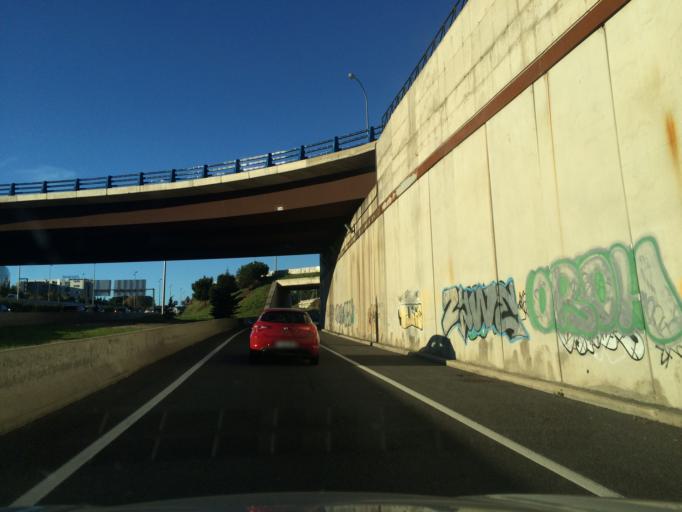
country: ES
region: Madrid
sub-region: Provincia de Madrid
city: Las Tablas
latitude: 40.4954
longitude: -3.6676
